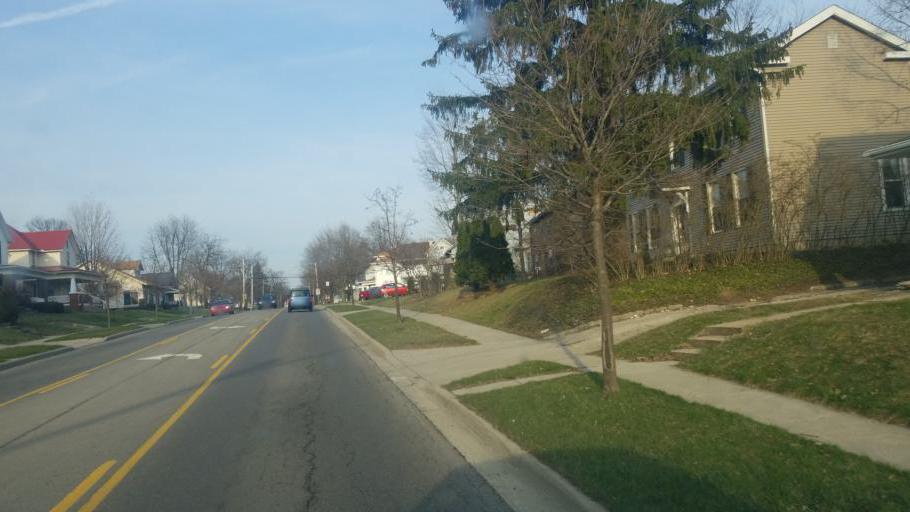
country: US
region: Ohio
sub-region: Logan County
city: Bellefontaine
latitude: 40.3626
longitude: -83.7532
